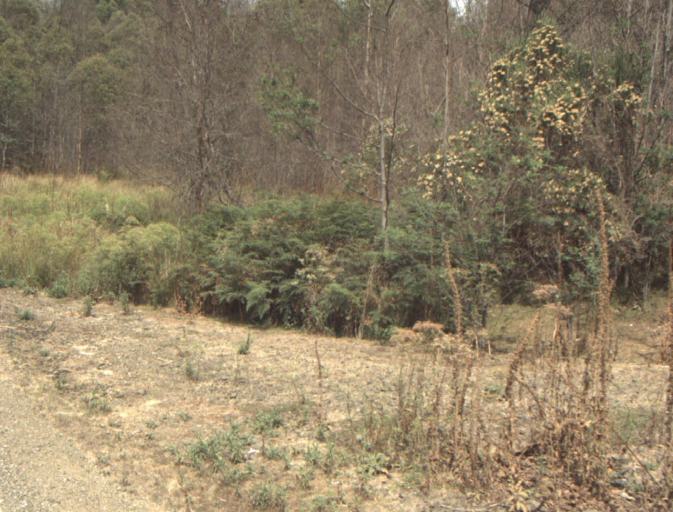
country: AU
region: Tasmania
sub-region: Launceston
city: Mayfield
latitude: -41.1964
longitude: 147.2627
